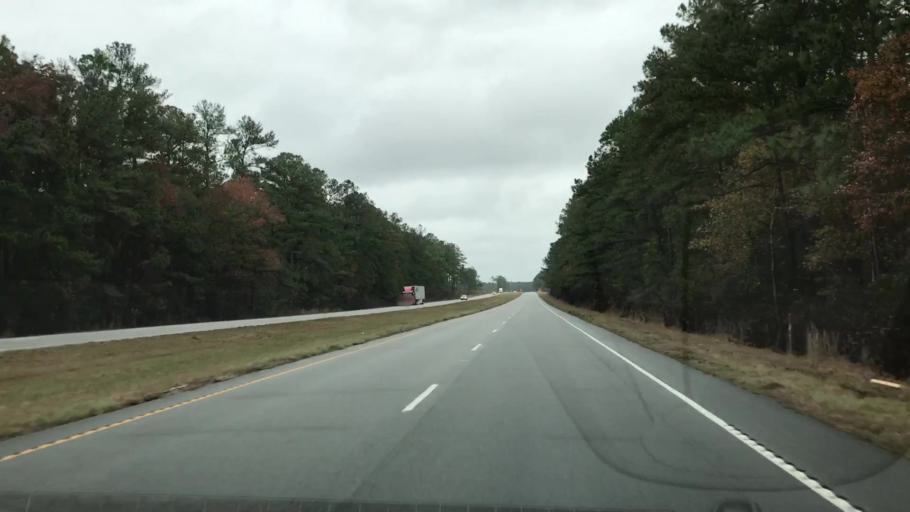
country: US
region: South Carolina
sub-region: Charleston County
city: Awendaw
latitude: 33.1660
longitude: -79.4225
